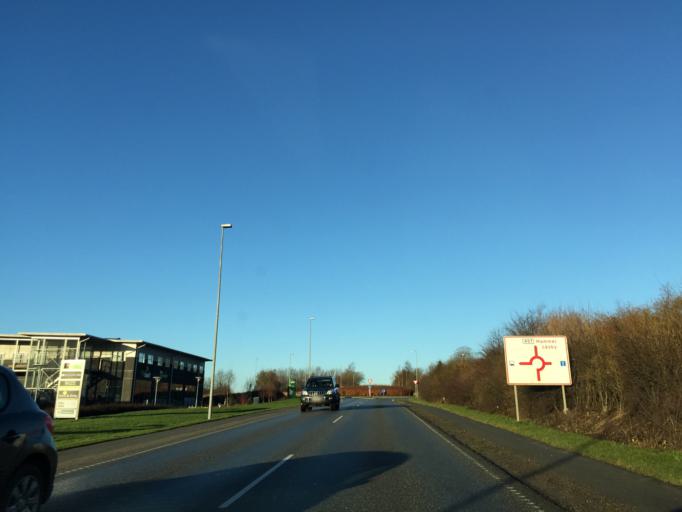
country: DK
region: Central Jutland
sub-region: Skanderborg Kommune
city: Skanderborg
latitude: 56.0463
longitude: 9.9200
